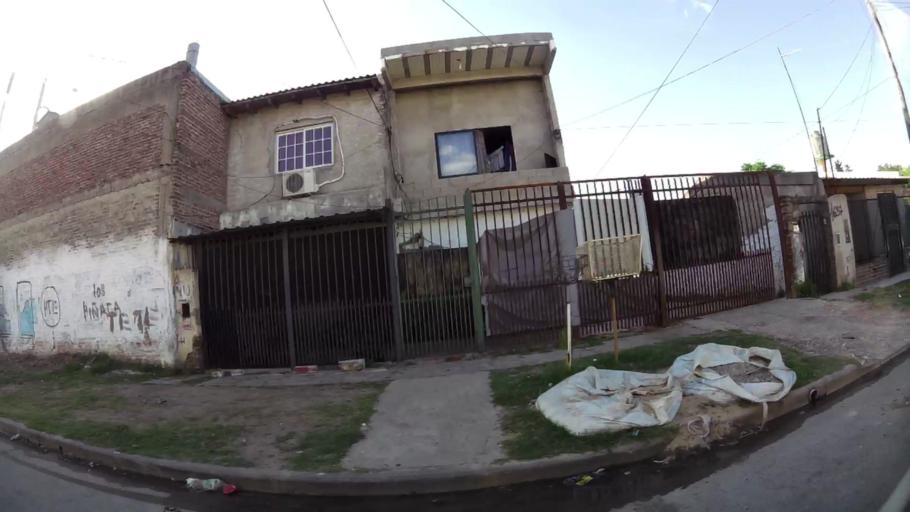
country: AR
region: Buenos Aires
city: Hurlingham
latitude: -34.5679
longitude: -58.6118
